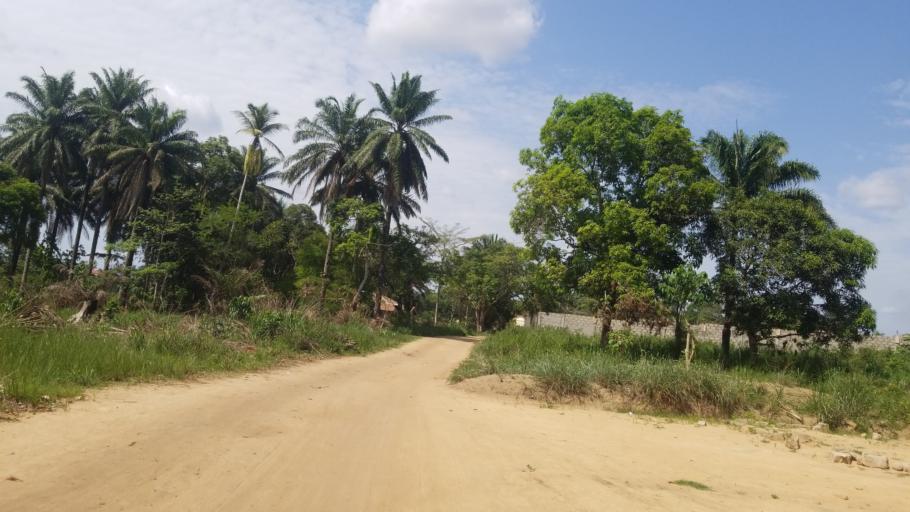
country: SL
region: Western Area
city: Waterloo
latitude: 8.3221
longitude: -13.0315
